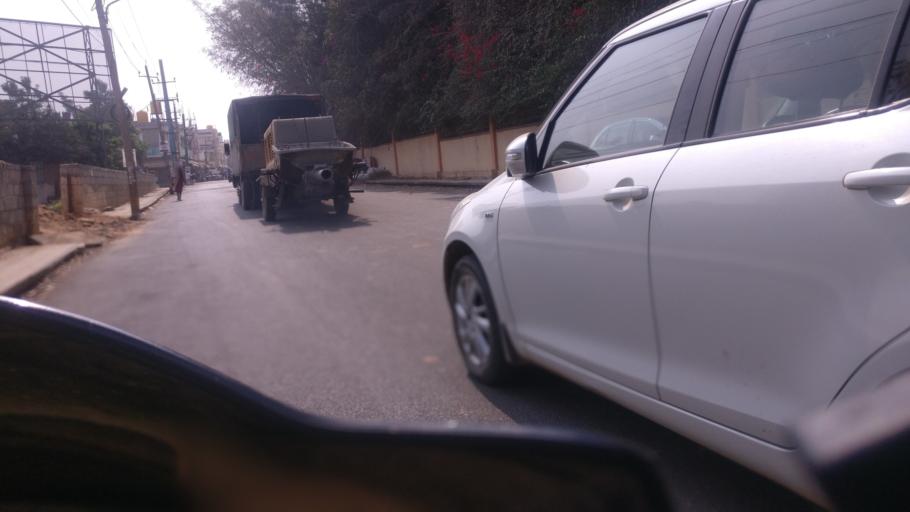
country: IN
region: Karnataka
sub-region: Bangalore Urban
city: Bangalore
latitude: 12.8949
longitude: 77.6767
